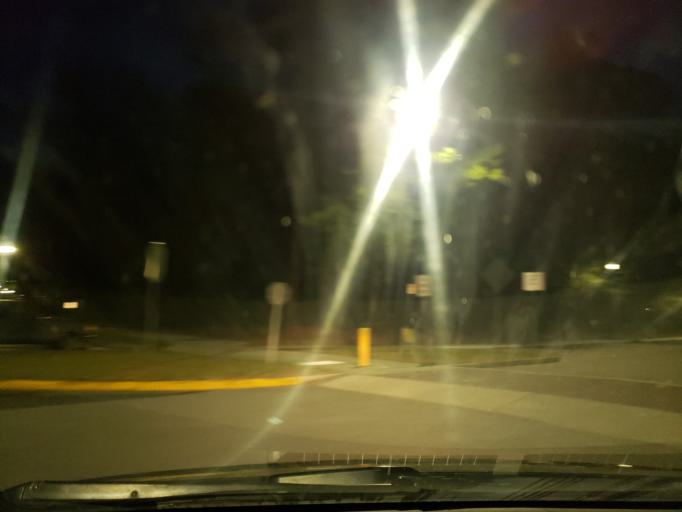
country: US
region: Georgia
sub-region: Chatham County
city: Montgomery
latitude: 31.9780
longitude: -81.1674
